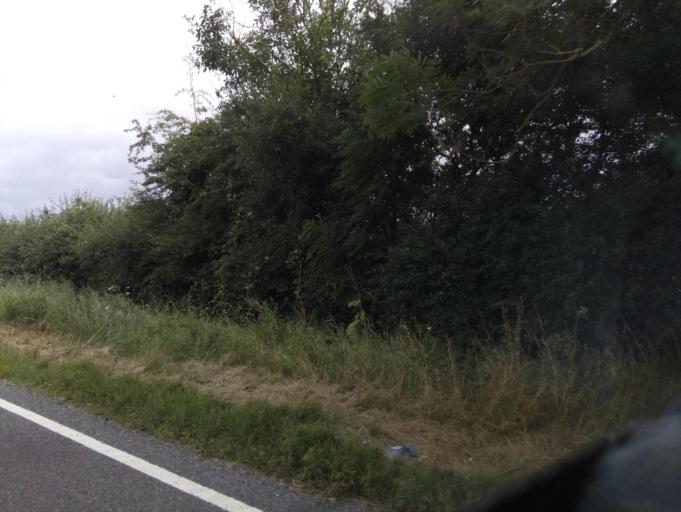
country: GB
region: England
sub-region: District of Rutland
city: Ryhall
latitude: 52.6884
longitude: -0.4821
